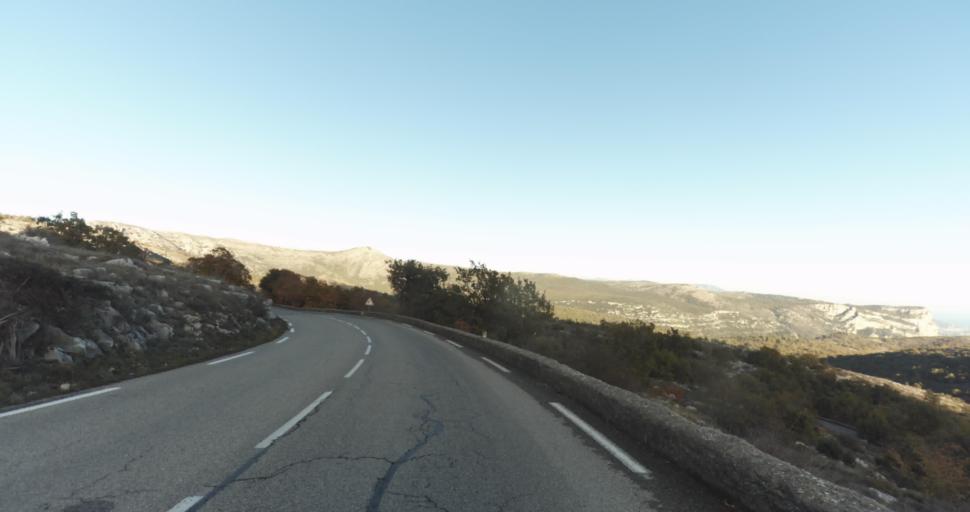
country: FR
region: Provence-Alpes-Cote d'Azur
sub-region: Departement des Alpes-Maritimes
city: Vence
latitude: 43.7620
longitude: 7.0837
